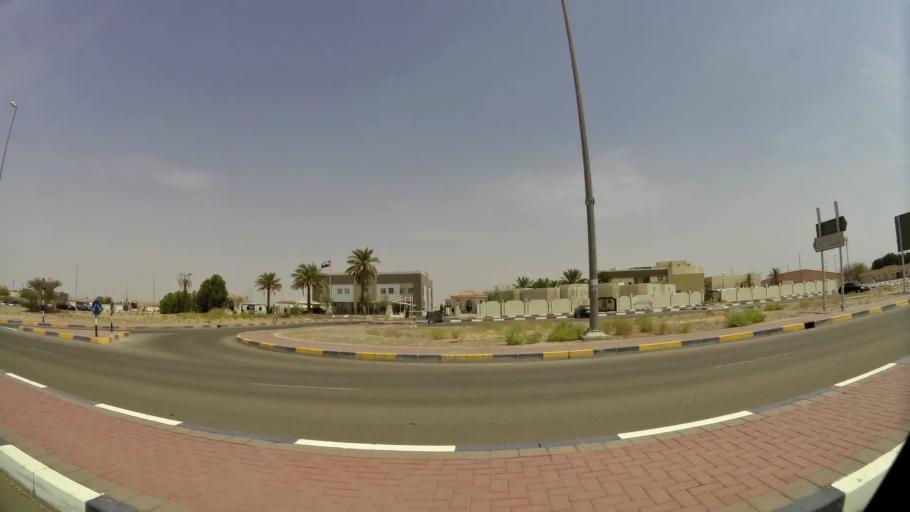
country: AE
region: Abu Dhabi
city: Al Ain
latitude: 24.1919
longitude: 55.7221
